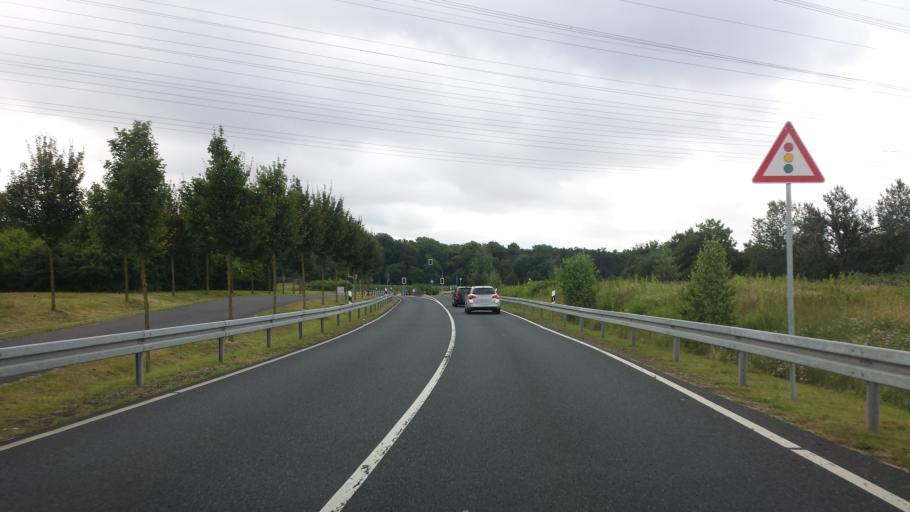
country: DE
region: Hesse
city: Kelsterbach
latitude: 50.0830
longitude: 8.5538
